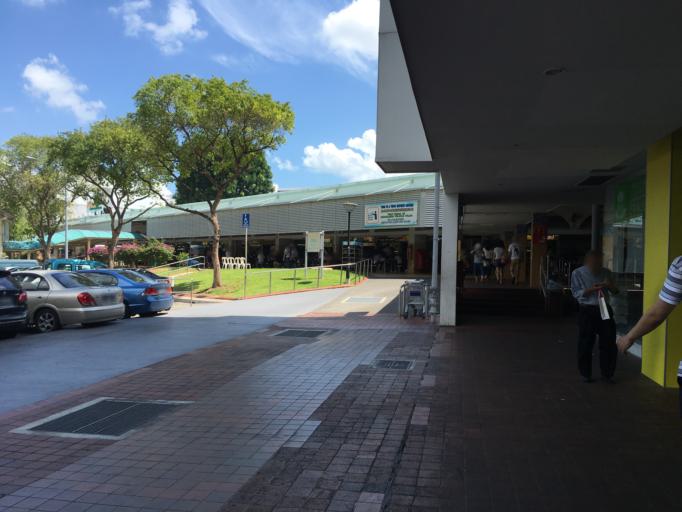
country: SG
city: Singapore
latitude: 1.3595
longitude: 103.8856
